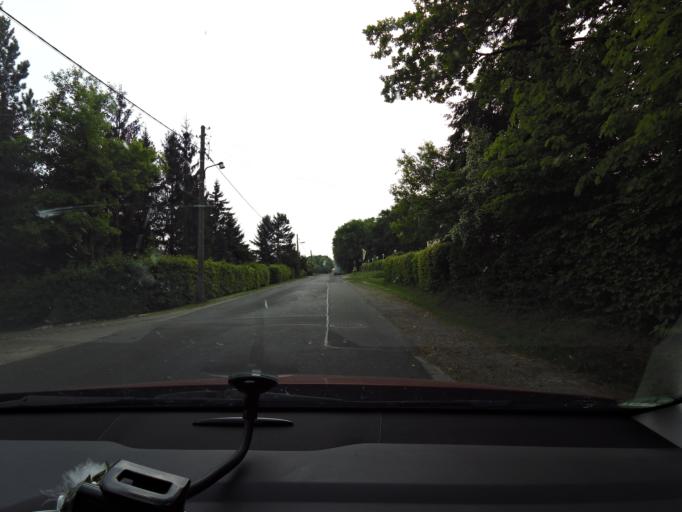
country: DE
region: Thuringia
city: Oberdorla
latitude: 51.2010
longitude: 10.3983
